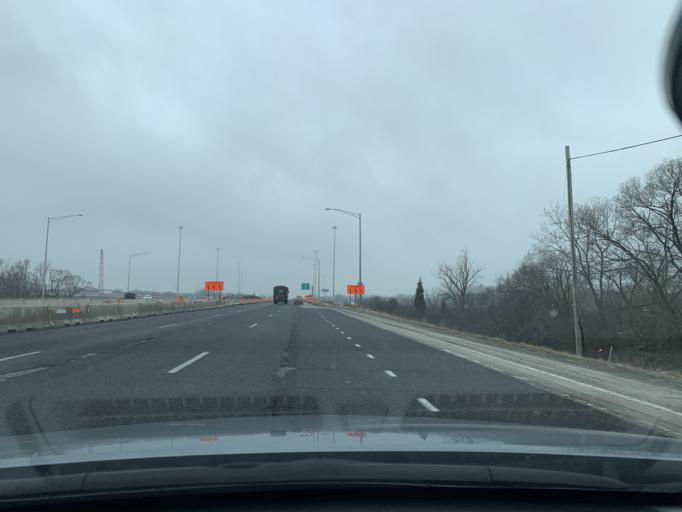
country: US
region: Illinois
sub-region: Cook County
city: Posen
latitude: 41.6213
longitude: -87.6839
